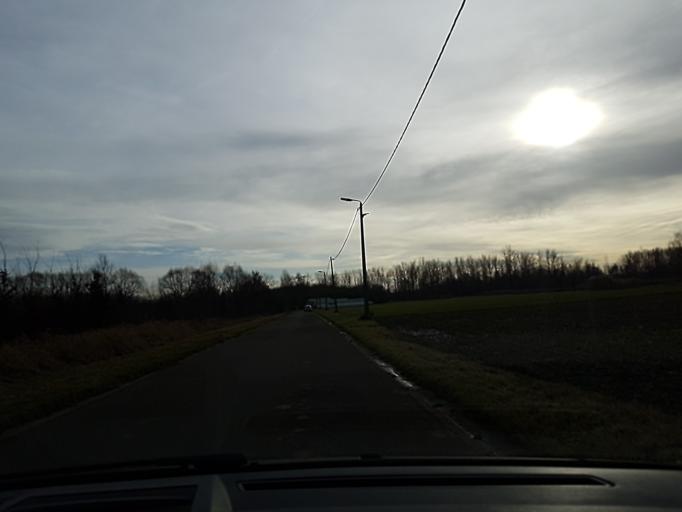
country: BE
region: Flanders
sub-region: Provincie Vlaams-Brabant
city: Rotselaar
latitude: 50.9427
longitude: 4.7077
